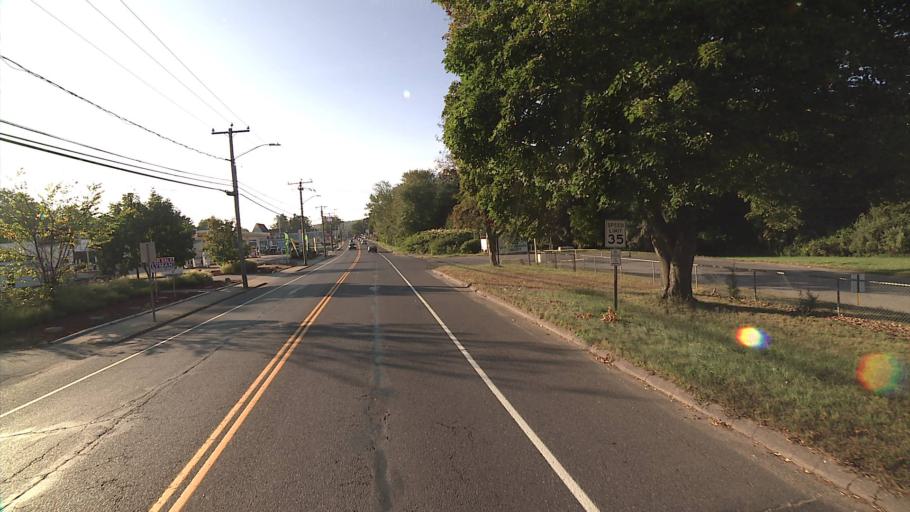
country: US
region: Connecticut
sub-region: Windham County
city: Willimantic
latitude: 41.7210
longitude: -72.2377
